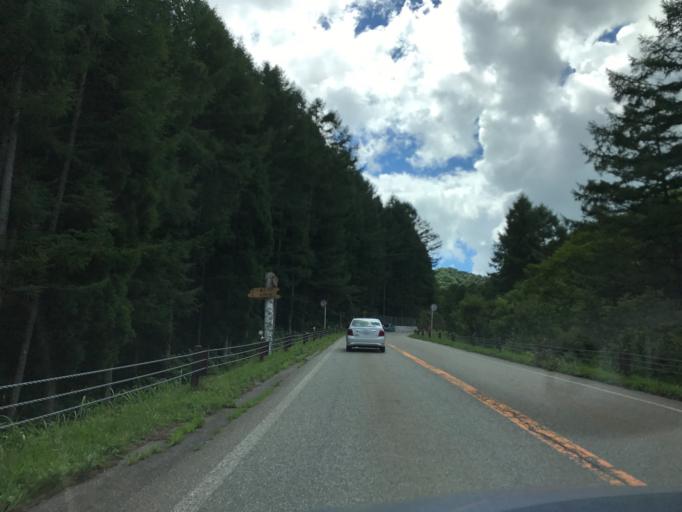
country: JP
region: Gifu
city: Takayama
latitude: 36.0391
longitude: 137.0802
